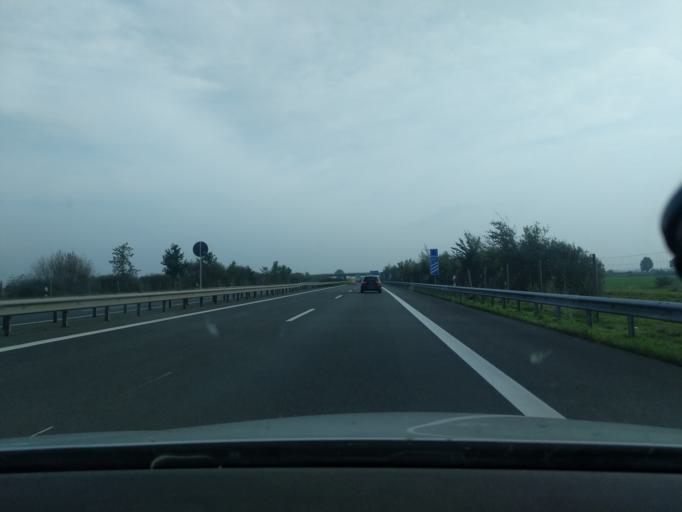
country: DE
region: Lower Saxony
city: Dollern
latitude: 53.5485
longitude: 9.5658
